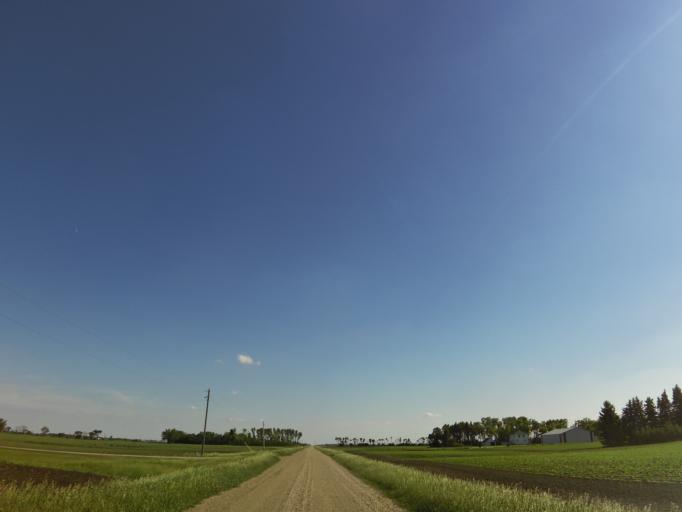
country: US
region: North Dakota
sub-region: Walsh County
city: Grafton
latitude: 48.3524
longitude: -97.2336
